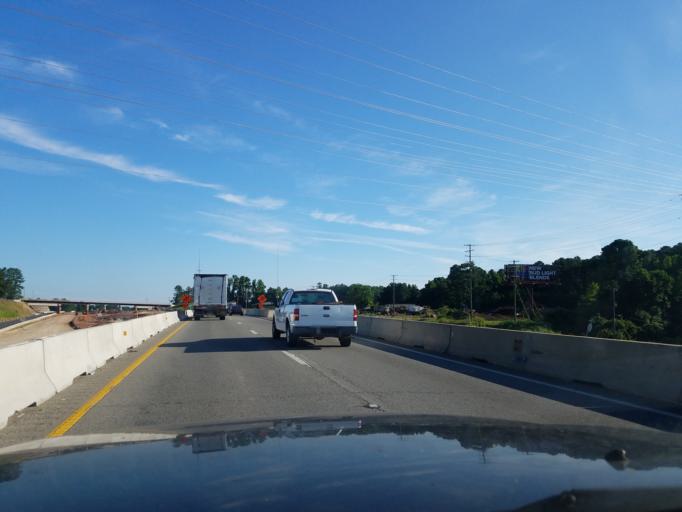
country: US
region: North Carolina
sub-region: Durham County
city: Durham
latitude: 35.9822
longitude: -78.8586
